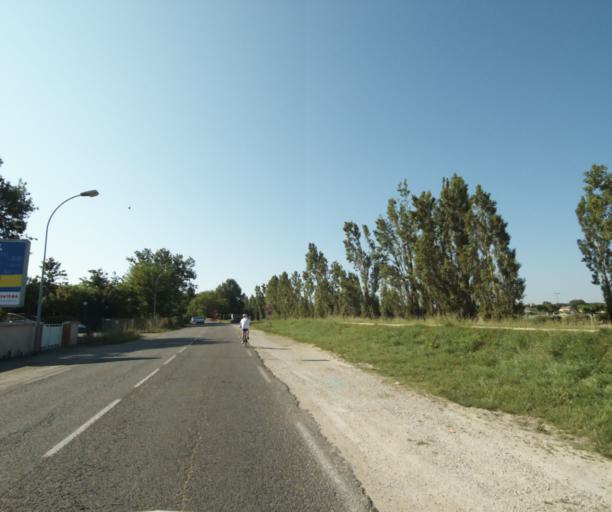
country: FR
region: Midi-Pyrenees
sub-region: Departement du Tarn-et-Garonne
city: Montauban
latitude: 44.0207
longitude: 1.3813
